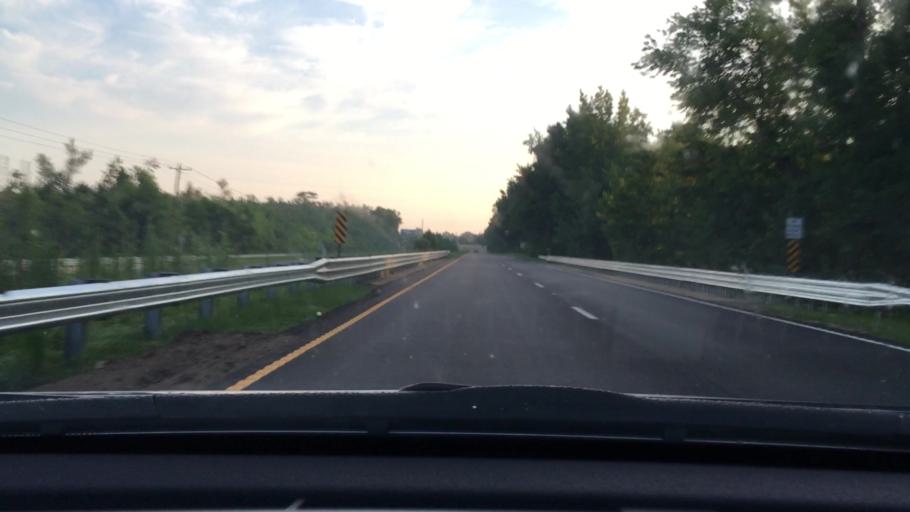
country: US
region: South Carolina
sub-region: Sumter County
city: Lakewood
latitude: 33.8752
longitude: -80.3522
